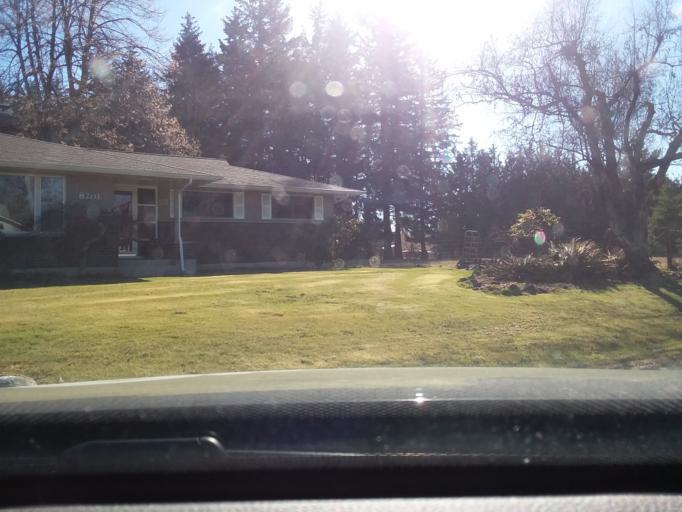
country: US
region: Washington
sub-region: Pierce County
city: Waller
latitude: 47.1825
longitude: -122.3838
